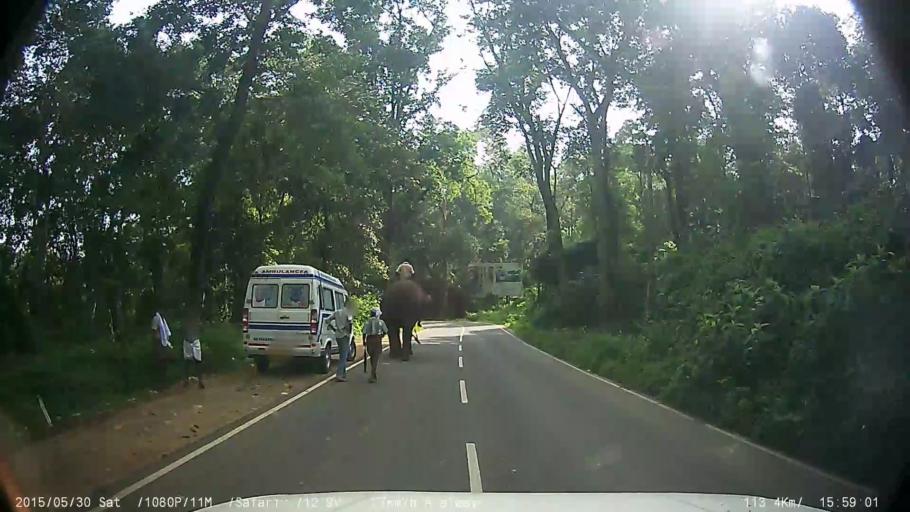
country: IN
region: Kerala
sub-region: Wayanad
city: Kalpetta
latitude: 11.6470
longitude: 76.0893
